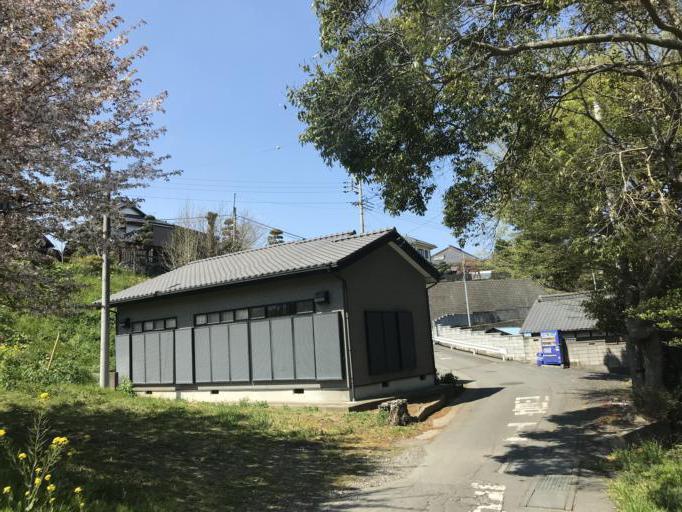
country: JP
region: Ibaraki
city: Moriya
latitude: 35.9235
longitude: 139.9907
